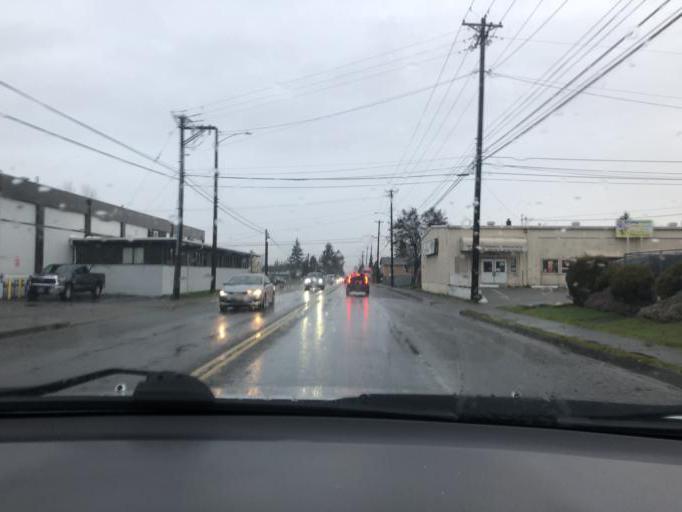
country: US
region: Washington
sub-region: Pierce County
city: Midland
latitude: 47.2020
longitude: -122.4209
